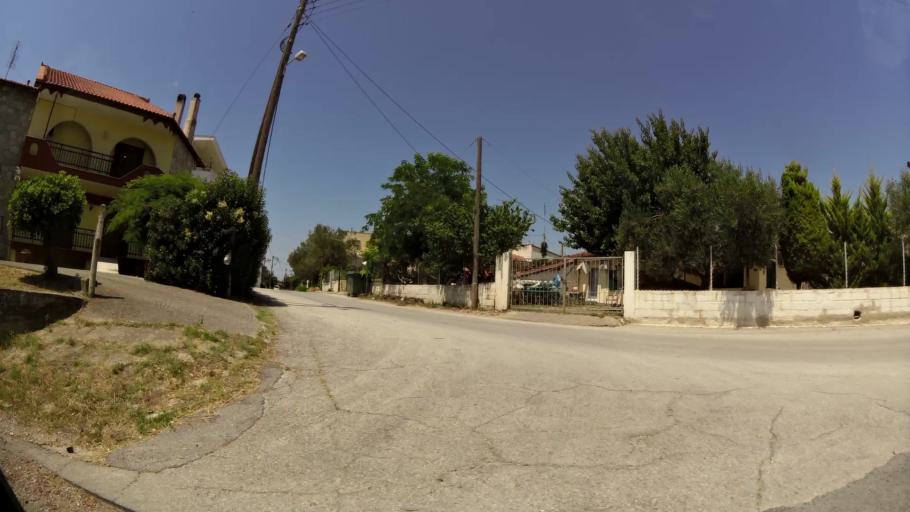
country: GR
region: Central Macedonia
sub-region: Nomos Thessalonikis
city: Epanomi
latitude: 40.4306
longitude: 22.9239
